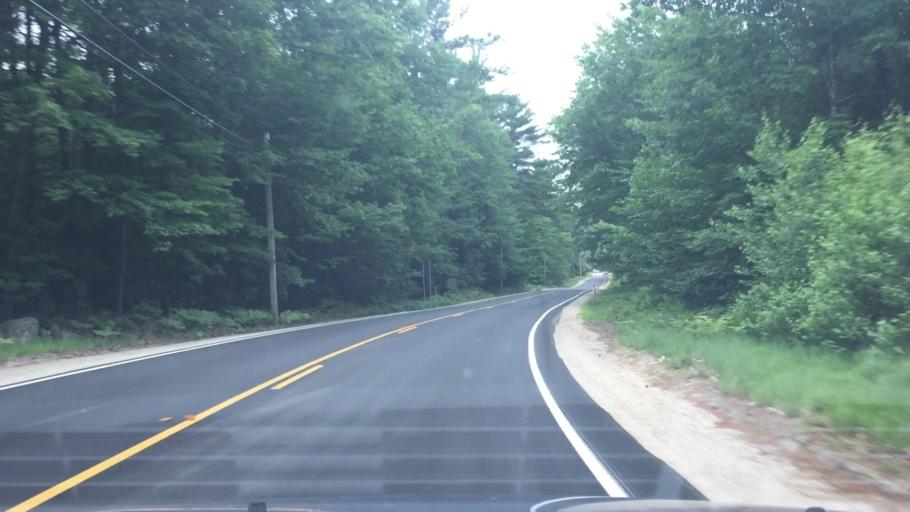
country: US
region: New Hampshire
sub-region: Carroll County
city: Freedom
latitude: 43.8188
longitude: -71.0668
